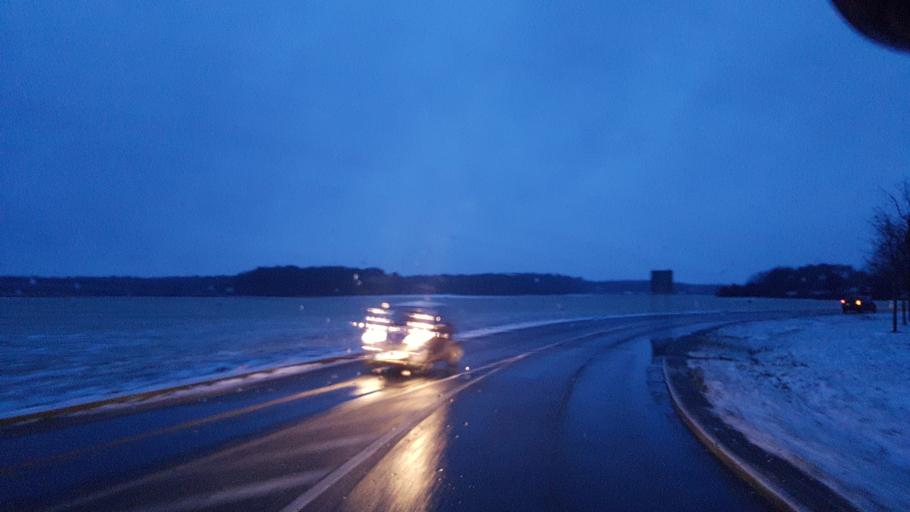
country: DE
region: Brandenburg
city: Briesen
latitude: 51.8032
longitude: 14.2496
